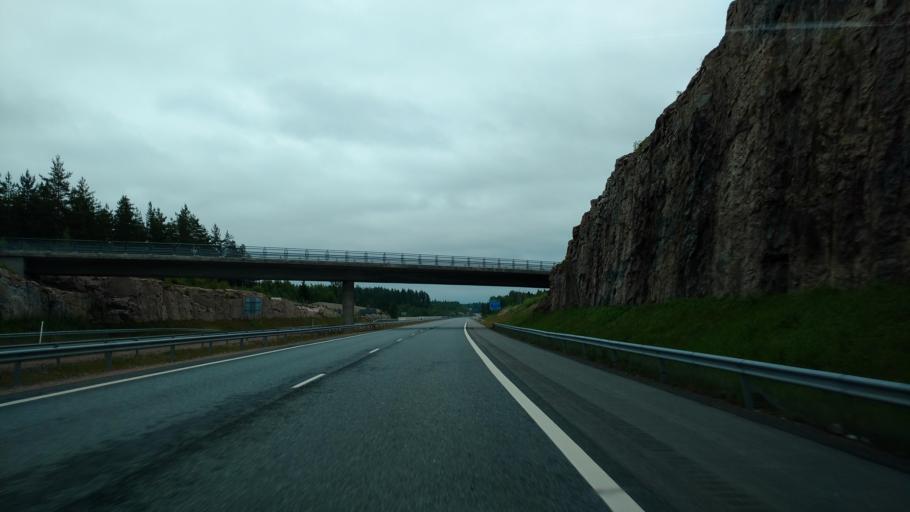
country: FI
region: Varsinais-Suomi
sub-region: Salo
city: Muurla
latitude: 60.3809
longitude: 23.4278
